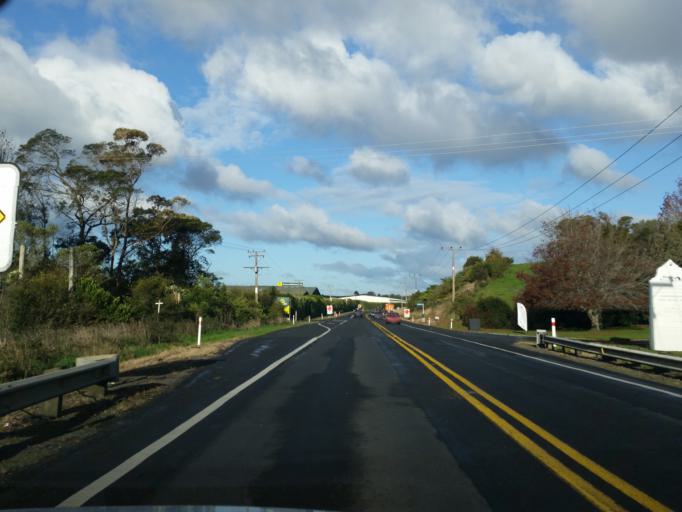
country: NZ
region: Bay of Plenty
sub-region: Western Bay of Plenty District
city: Katikati
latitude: -37.6074
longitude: 175.9418
